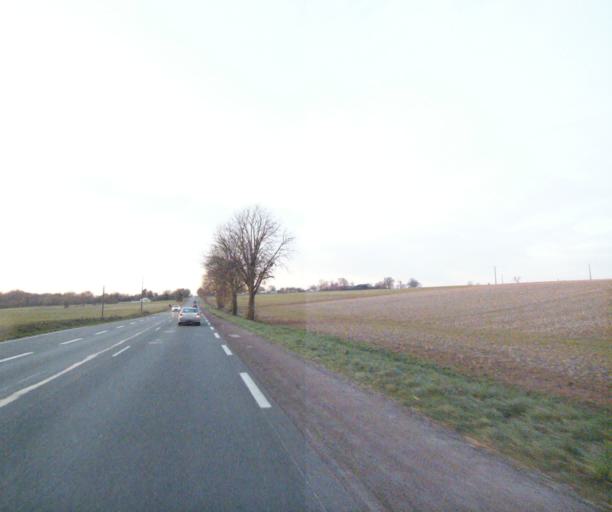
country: FR
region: Poitou-Charentes
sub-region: Departement de la Charente-Maritime
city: Saint-Georges-des-Coteaux
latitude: 45.7822
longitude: -0.7092
